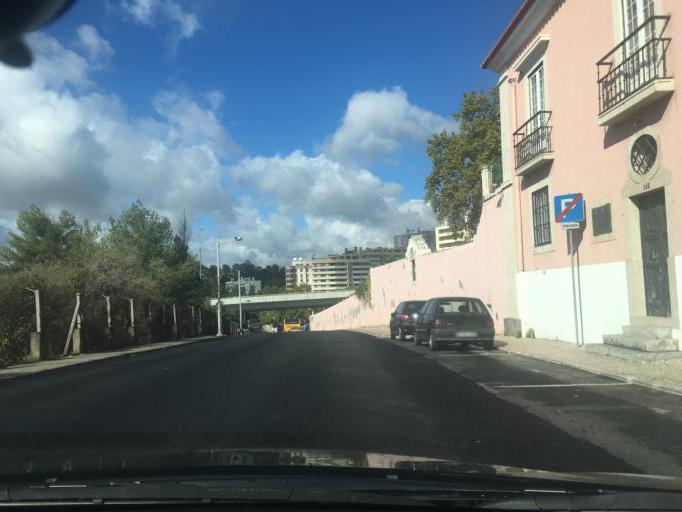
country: PT
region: Lisbon
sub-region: Lisbon
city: Lisbon
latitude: 38.7421
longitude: -9.1645
